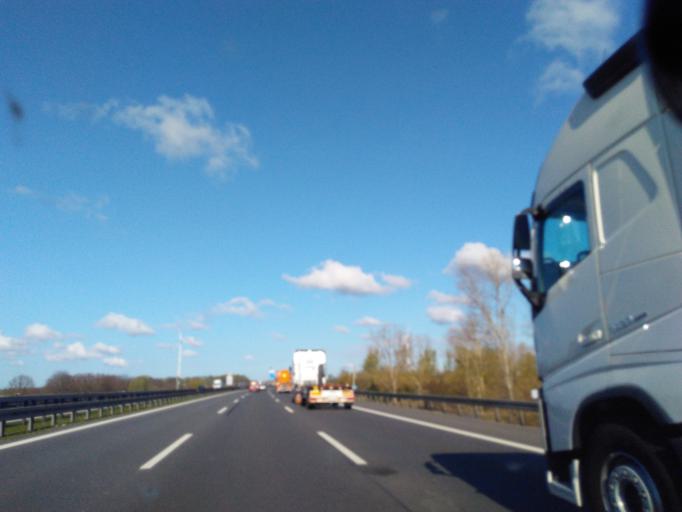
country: DE
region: Berlin
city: Buchholz
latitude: 52.6322
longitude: 13.4522
